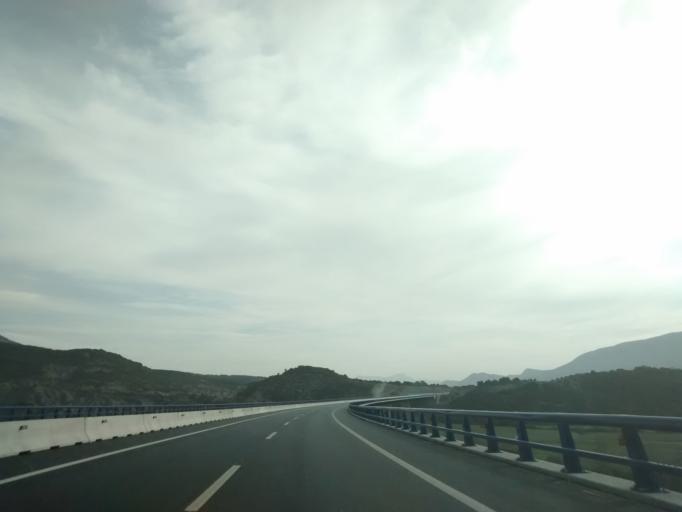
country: ES
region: Aragon
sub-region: Provincia de Zaragoza
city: Siguees
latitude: 42.6255
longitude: -1.0158
